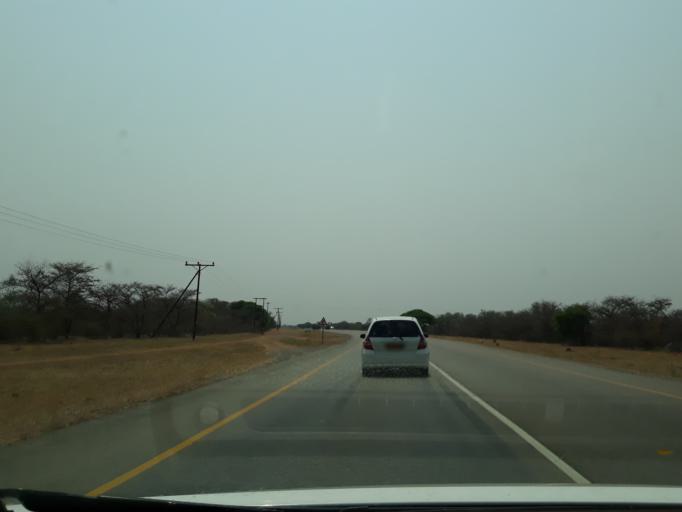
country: BW
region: Kgatleng
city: Mochudi
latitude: -24.2929
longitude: 26.1327
